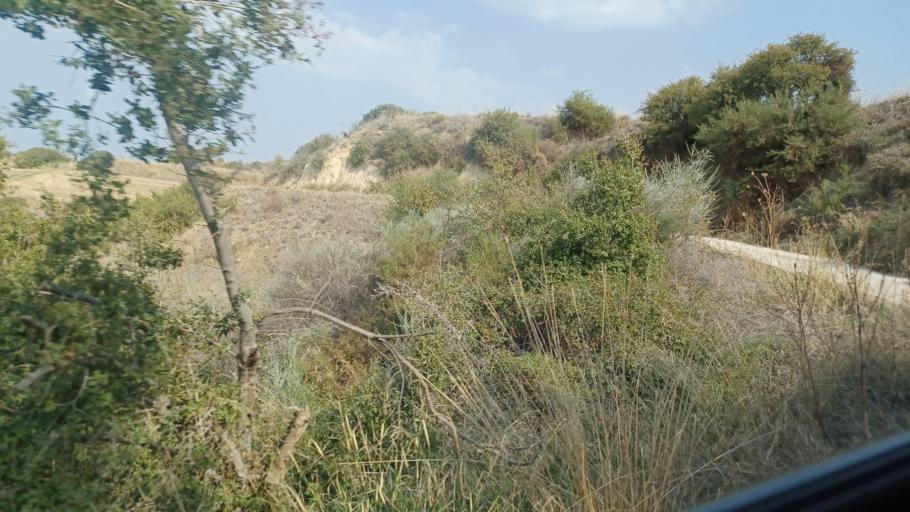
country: CY
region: Pafos
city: Polis
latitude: 34.9887
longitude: 32.4584
